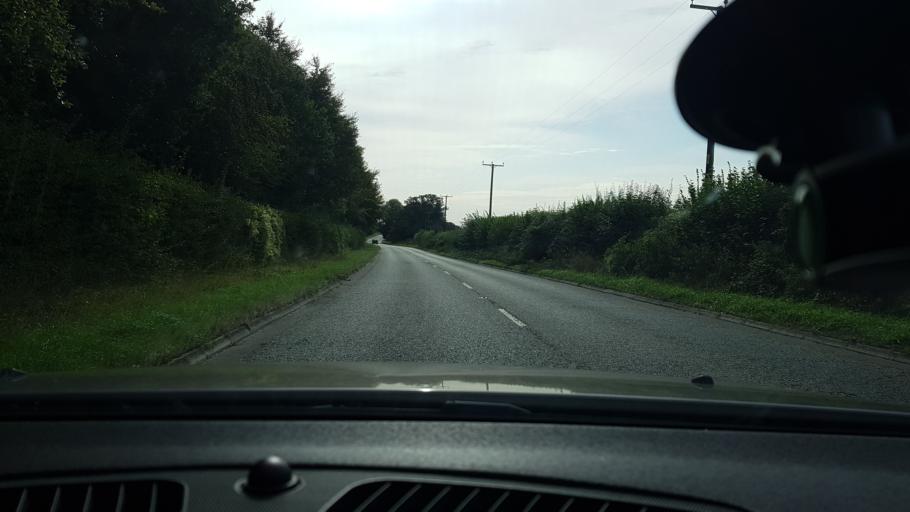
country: GB
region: England
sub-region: West Berkshire
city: Wickham
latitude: 51.4558
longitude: -1.4707
